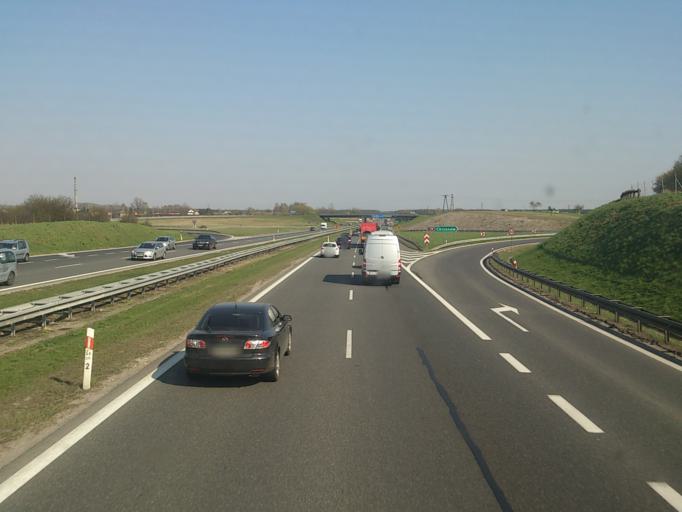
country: PL
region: Lesser Poland Voivodeship
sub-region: Powiat chrzanowski
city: Chrzanow
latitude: 50.1493
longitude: 19.4226
